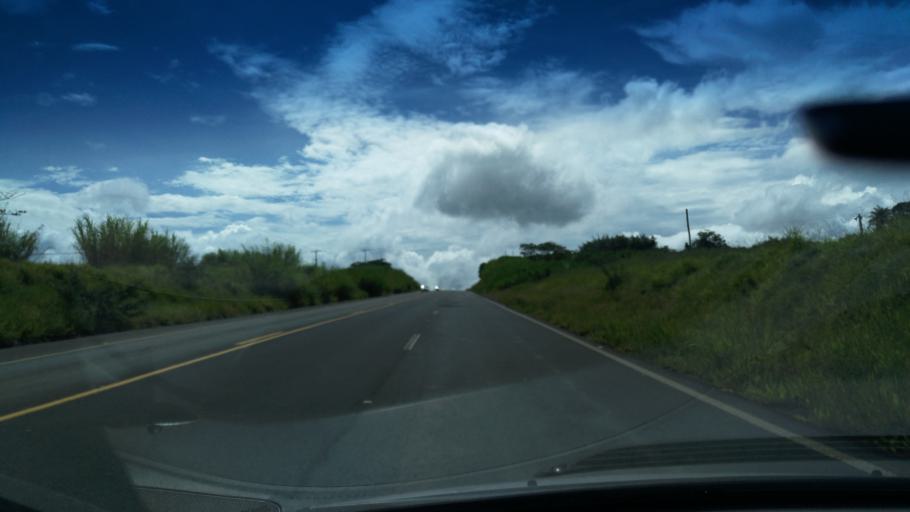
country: BR
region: Sao Paulo
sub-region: Santo Antonio Do Jardim
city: Espirito Santo do Pinhal
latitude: -22.1557
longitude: -46.7253
